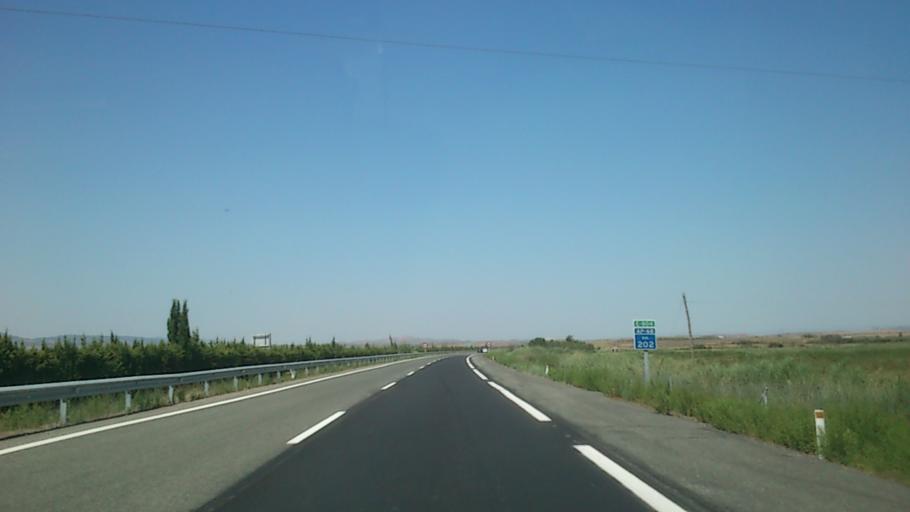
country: ES
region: Navarre
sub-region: Provincia de Navarra
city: Corella
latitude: 42.1369
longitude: -1.7757
